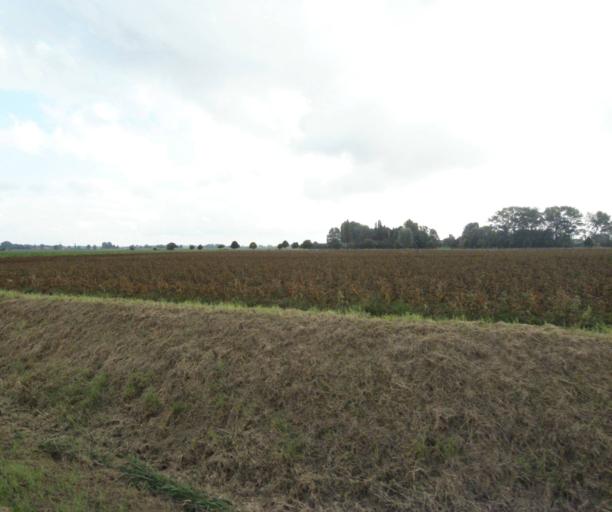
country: FR
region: Nord-Pas-de-Calais
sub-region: Departement du Nord
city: Herlies
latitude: 50.5908
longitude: 2.8517
